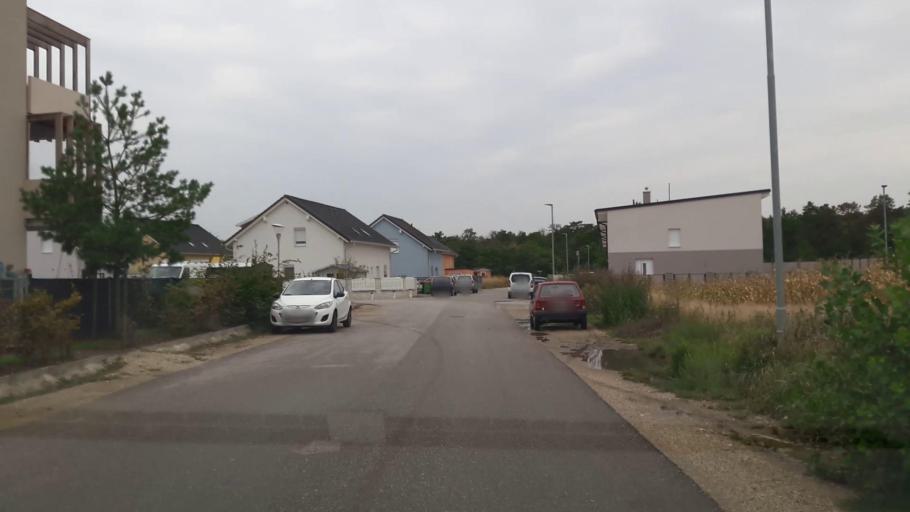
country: AT
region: Lower Austria
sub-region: Politischer Bezirk Ganserndorf
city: Strasshof an der Nordbahn
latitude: 48.3248
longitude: 16.6475
